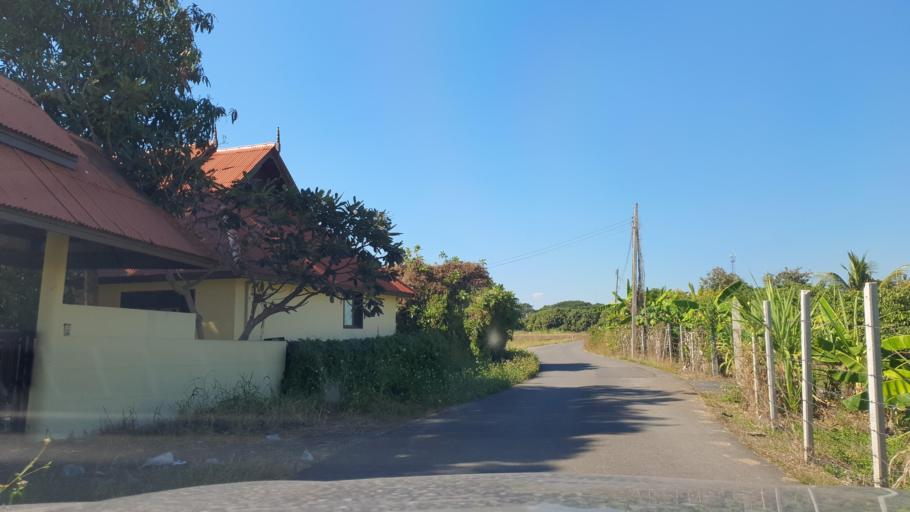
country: TH
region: Chiang Mai
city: San Pa Tong
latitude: 18.6494
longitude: 98.8681
